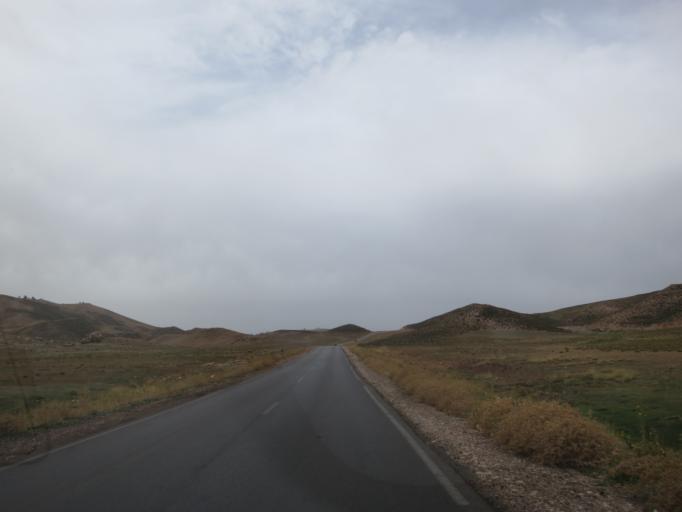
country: MA
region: Meknes-Tafilalet
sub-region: Khenifra
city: Itzer
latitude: 33.0538
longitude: -5.0414
